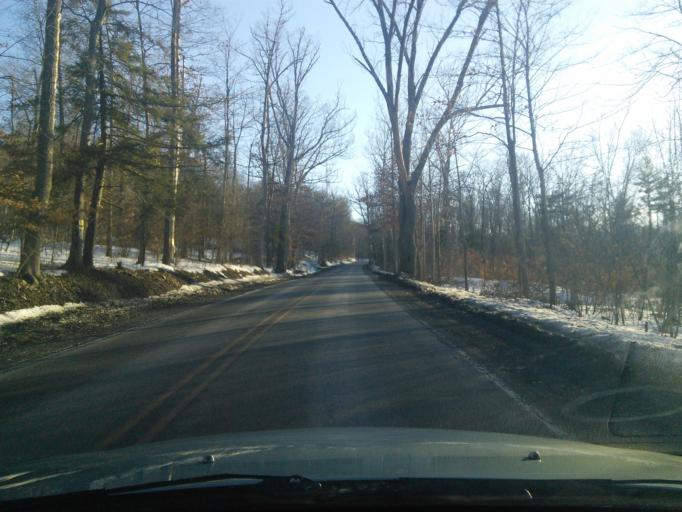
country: US
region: Pennsylvania
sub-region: Centre County
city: Park Forest Village
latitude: 40.8604
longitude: -77.9333
